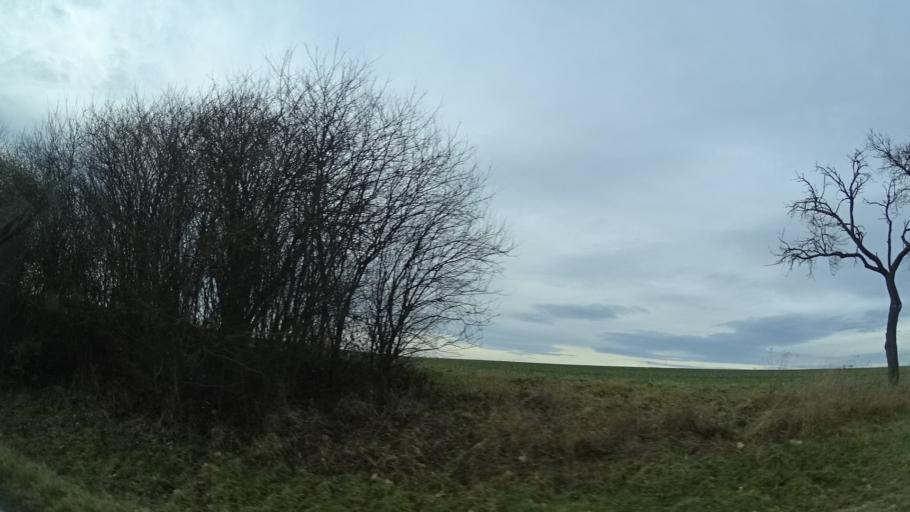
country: DE
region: Thuringia
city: Langenwolschendorf
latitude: 50.6687
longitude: 11.9452
